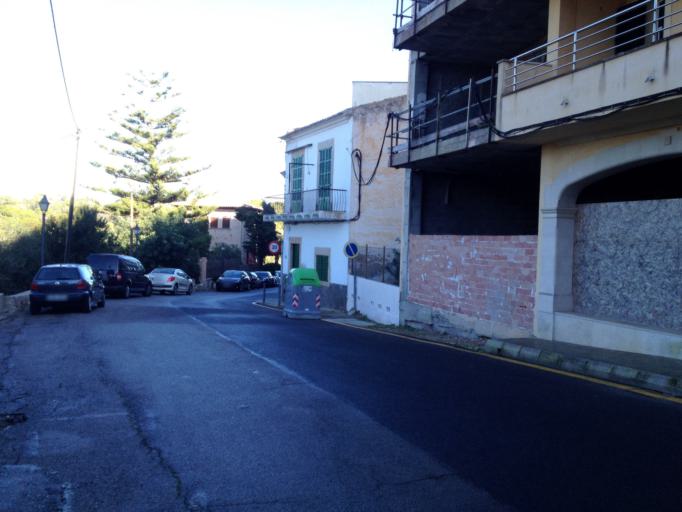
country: ES
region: Balearic Islands
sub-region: Illes Balears
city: Santanyi
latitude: 39.3310
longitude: 3.1688
